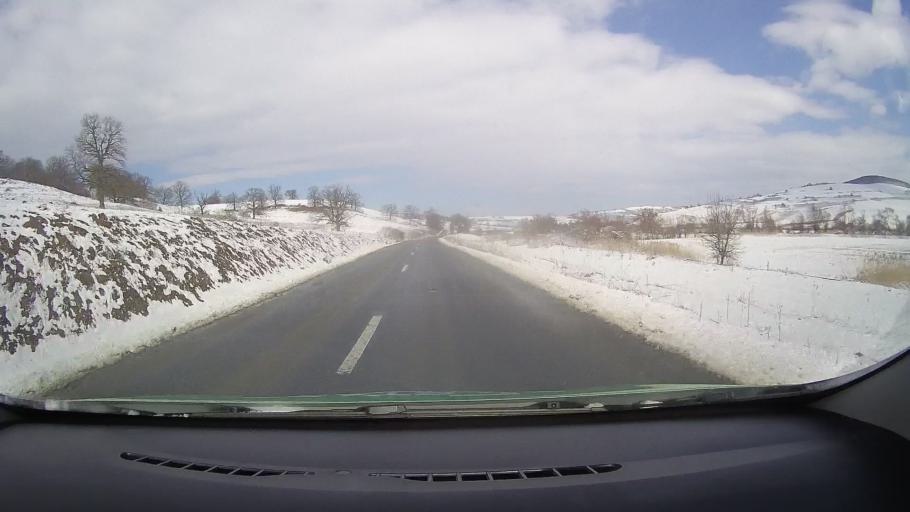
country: RO
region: Sibiu
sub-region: Comuna Altina
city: Altina
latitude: 45.9493
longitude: 24.4514
